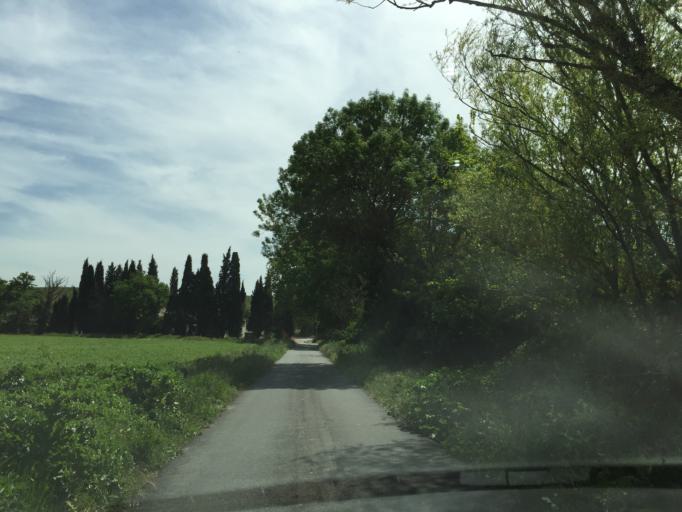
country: FR
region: Provence-Alpes-Cote d'Azur
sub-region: Departement du Vaucluse
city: Orange
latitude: 44.1224
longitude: 4.8459
